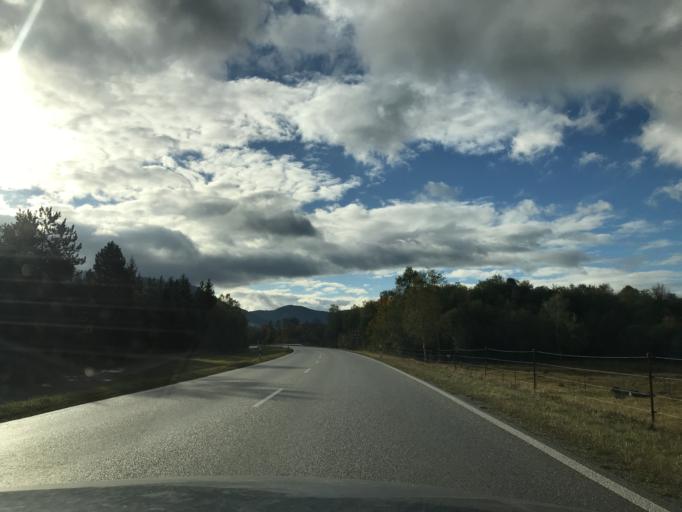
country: DE
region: Bavaria
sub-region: Upper Bavaria
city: Lenggries
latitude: 47.6919
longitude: 11.5659
